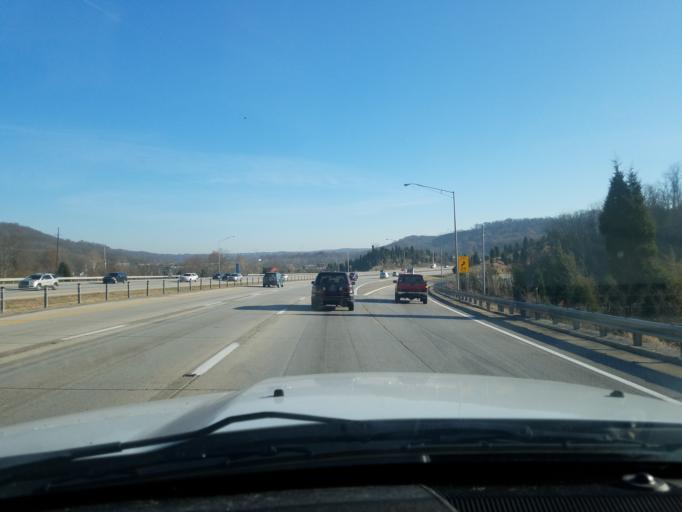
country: US
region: Kentucky
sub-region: Kenton County
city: Fort Wright
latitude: 39.0285
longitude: -84.5415
